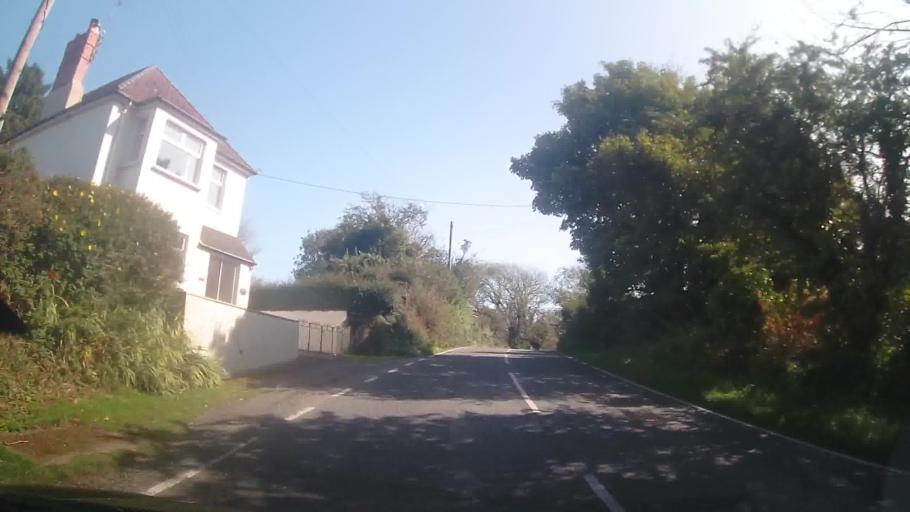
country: GB
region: Wales
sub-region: Pembrokeshire
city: Scleddau
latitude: 51.9356
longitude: -5.0145
